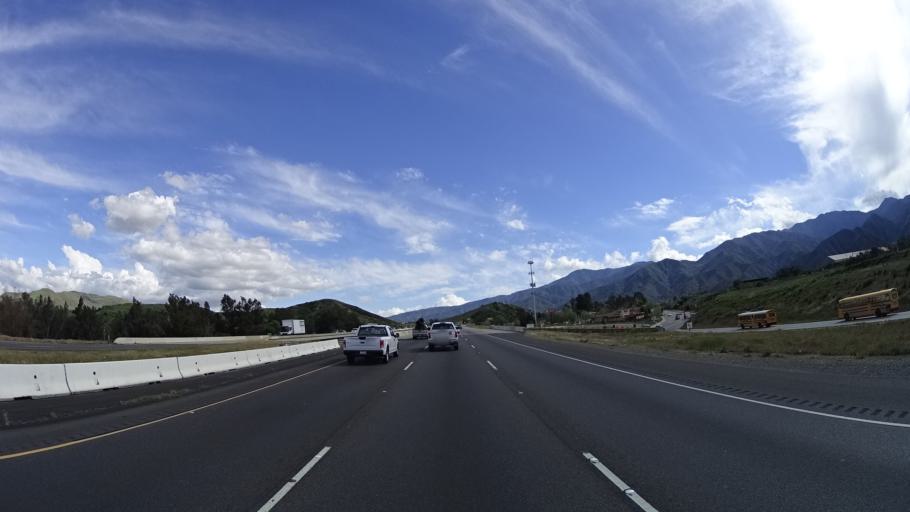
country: US
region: California
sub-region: Riverside County
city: El Cerrito
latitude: 33.7775
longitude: -117.4879
